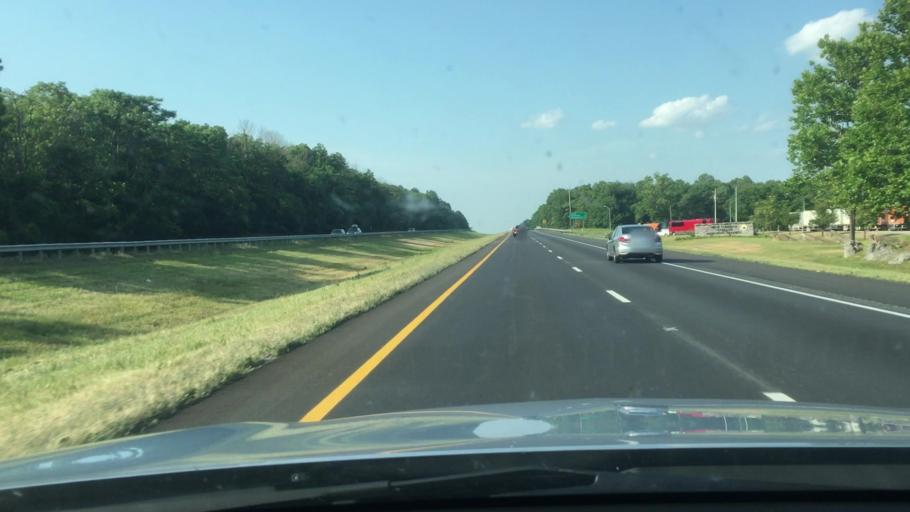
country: US
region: West Virginia
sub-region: Berkeley County
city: Inwood
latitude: 39.3192
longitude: -78.0729
